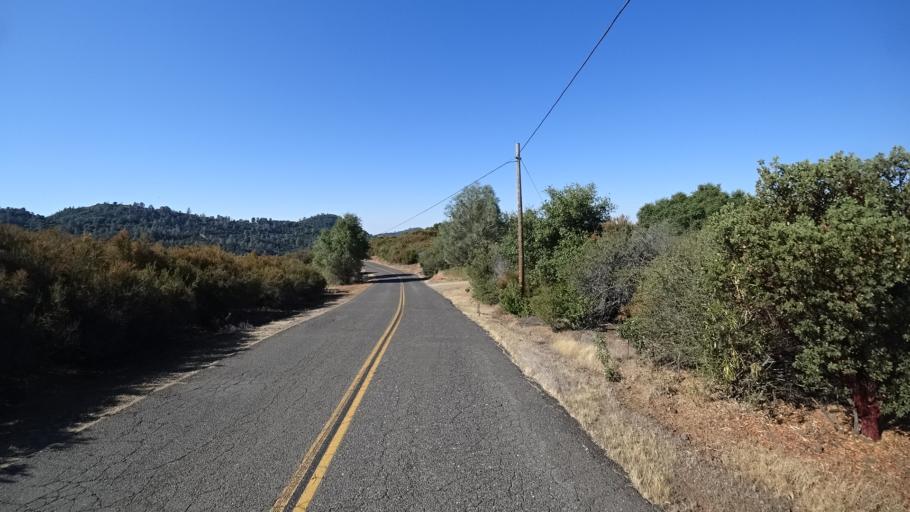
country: US
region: California
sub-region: Calaveras County
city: Murphys
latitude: 38.0728
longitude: -120.4648
